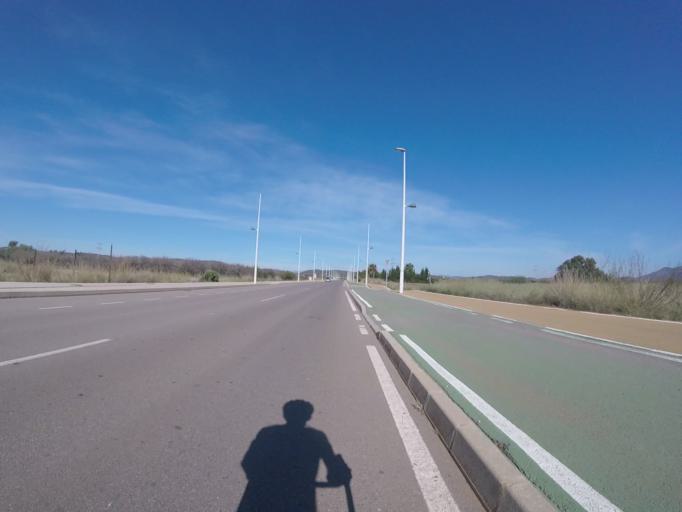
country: ES
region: Valencia
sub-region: Provincia de Castello
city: Torreblanca
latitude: 40.2135
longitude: 0.2226
